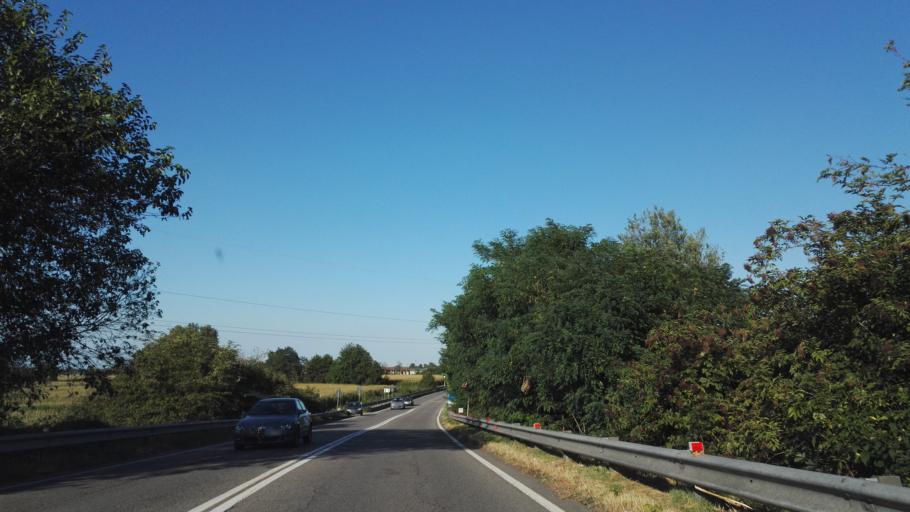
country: IT
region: Lombardy
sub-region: Citta metropolitana di Milano
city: Locate di Triulzi
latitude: 45.3617
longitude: 9.2324
